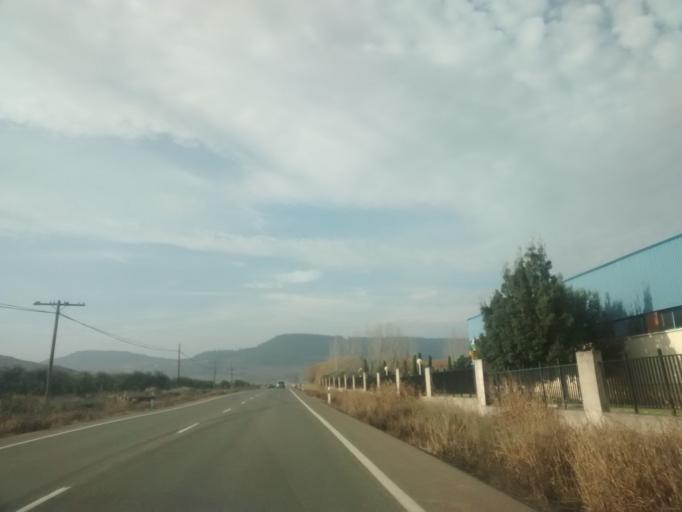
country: ES
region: La Rioja
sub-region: Provincia de La Rioja
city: Fuenmayor
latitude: 42.4642
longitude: -2.5989
